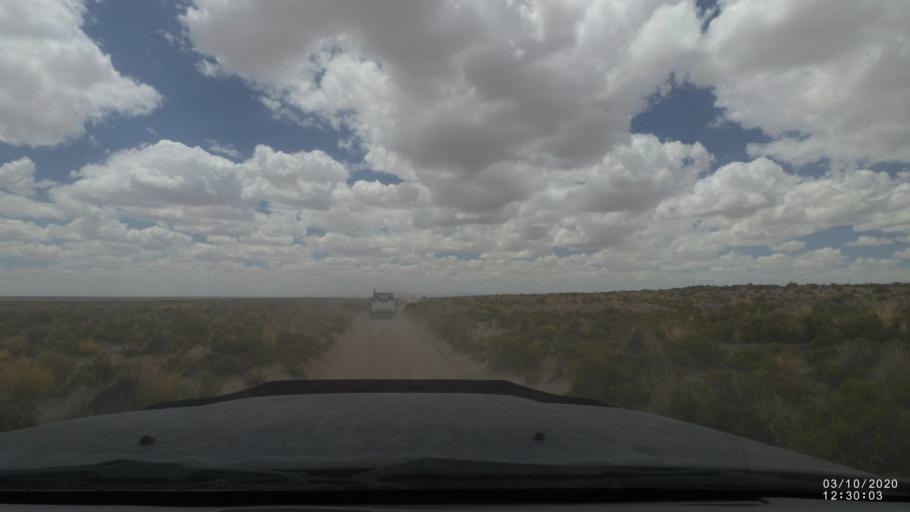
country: BO
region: Oruro
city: Poopo
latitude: -18.6879
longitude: -67.5453
